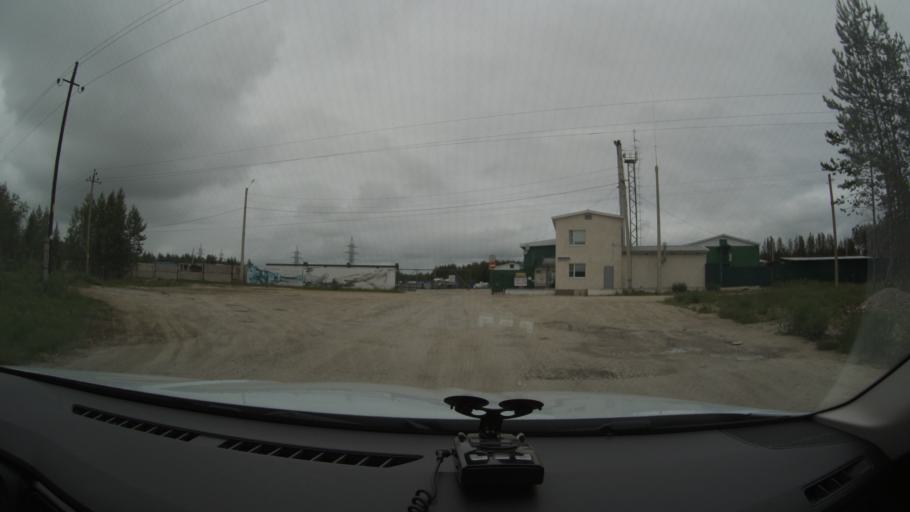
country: RU
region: Komi Republic
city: Kozhva
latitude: 65.1100
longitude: 57.0094
